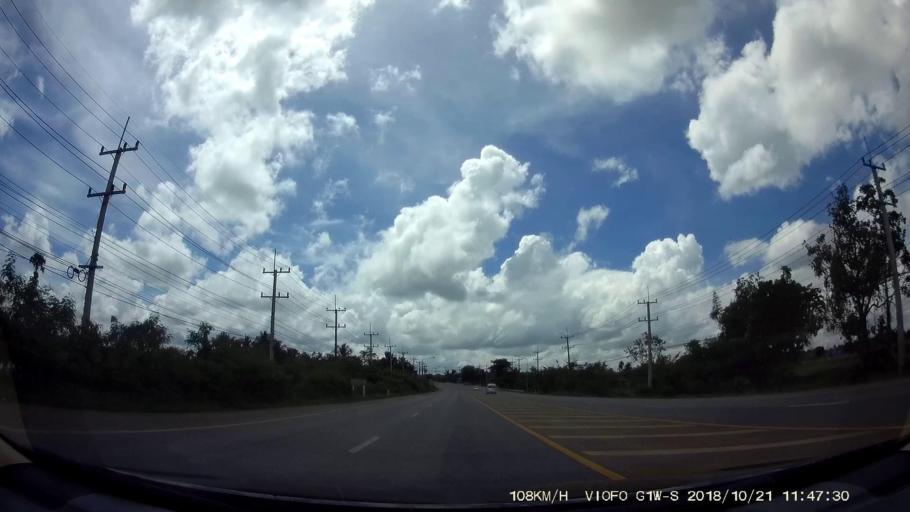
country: TH
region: Chaiyaphum
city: Noen Sa-nga
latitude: 15.6604
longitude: 101.9534
